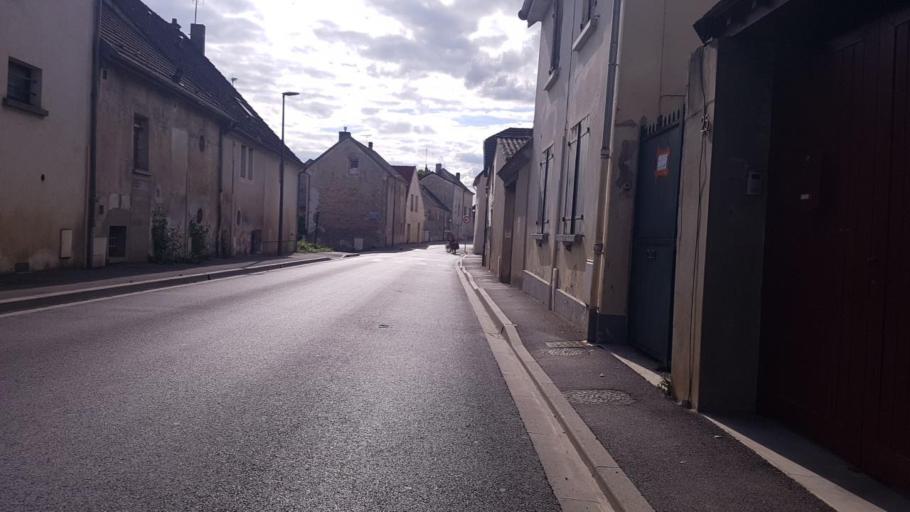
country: FR
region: Picardie
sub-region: Departement de l'Aisne
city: Brasles
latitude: 49.0477
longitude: 3.4301
